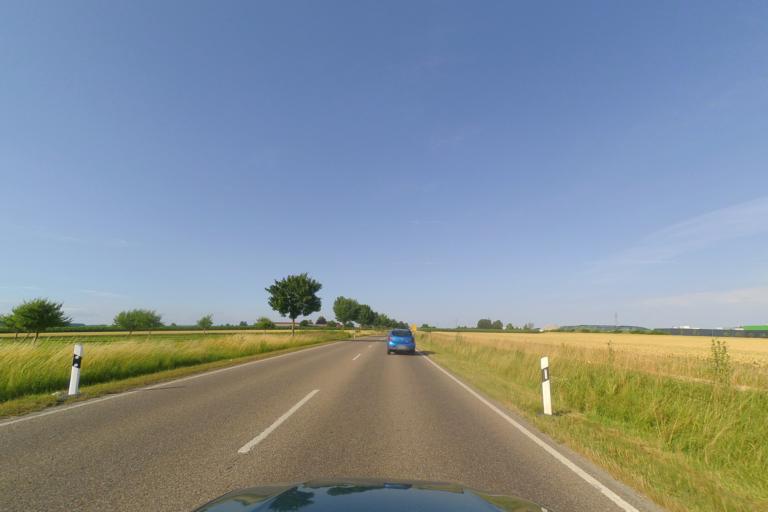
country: DE
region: Bavaria
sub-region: Swabia
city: Lauingen
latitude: 48.5731
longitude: 10.4052
